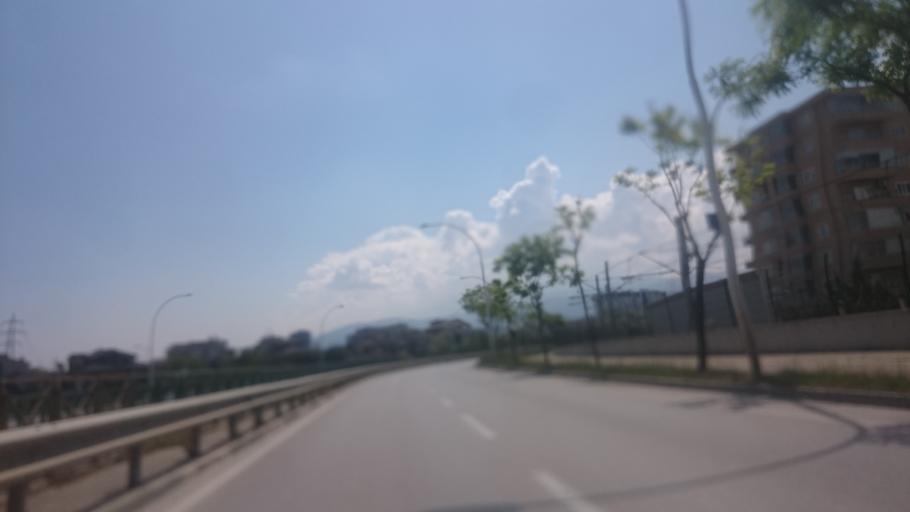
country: TR
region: Bursa
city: Cali
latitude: 40.2186
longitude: 28.9287
